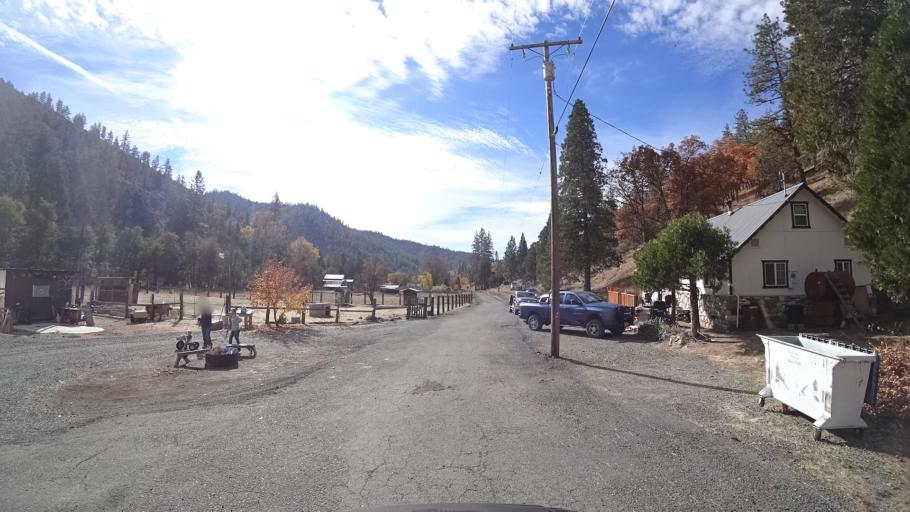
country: US
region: California
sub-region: Siskiyou County
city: Yreka
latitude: 41.6412
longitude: -122.7510
